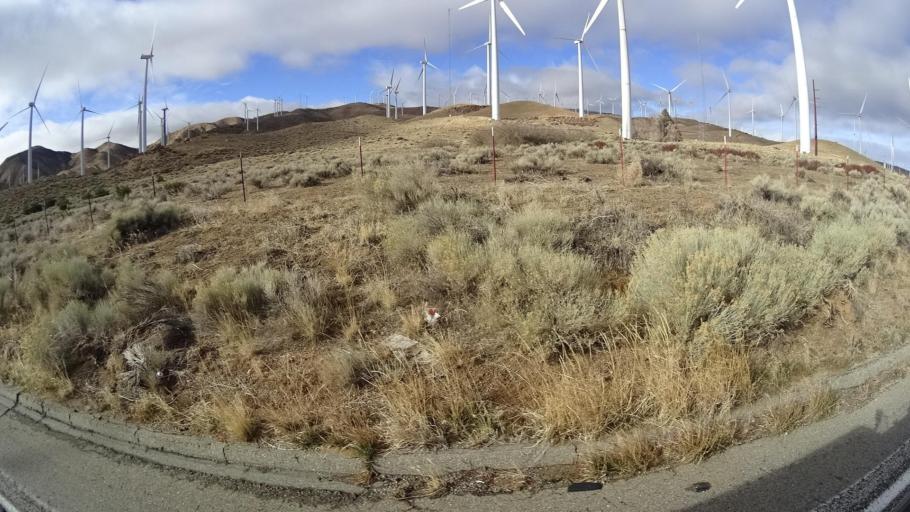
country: US
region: California
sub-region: Kern County
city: Tehachapi
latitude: 35.0378
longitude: -118.3525
